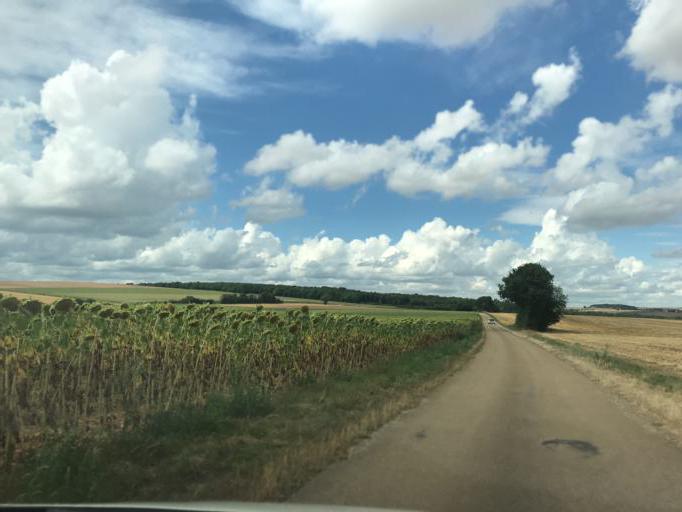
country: FR
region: Bourgogne
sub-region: Departement de l'Yonne
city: Fontenailles
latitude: 47.5810
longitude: 3.3451
